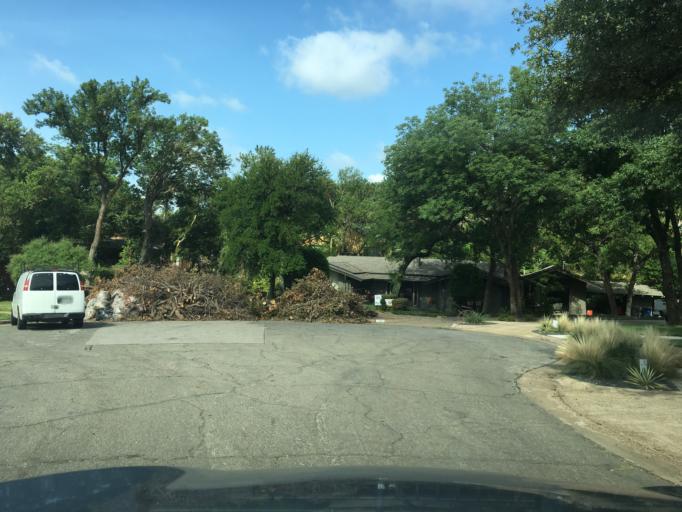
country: US
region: Texas
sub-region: Dallas County
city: Richardson
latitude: 32.9286
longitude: -96.7780
